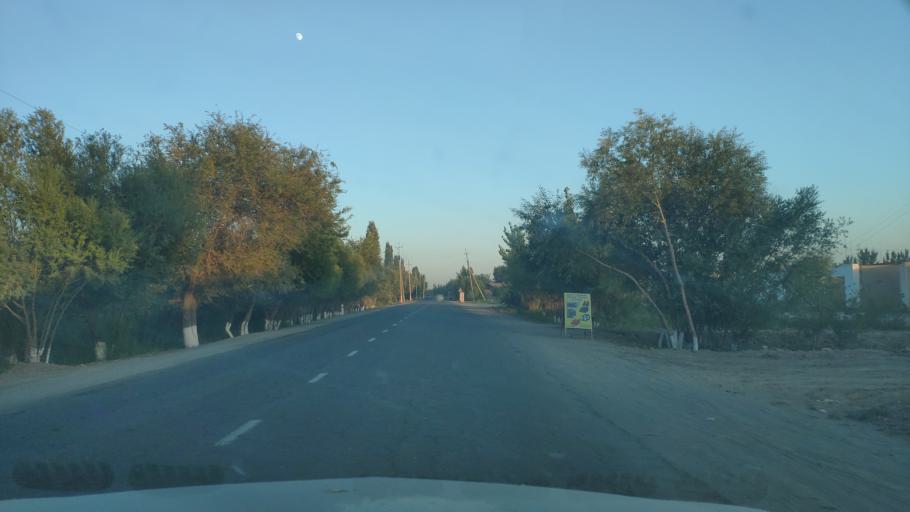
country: UZ
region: Karakalpakstan
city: To'rtko'l Shahri
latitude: 41.5652
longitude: 60.9530
